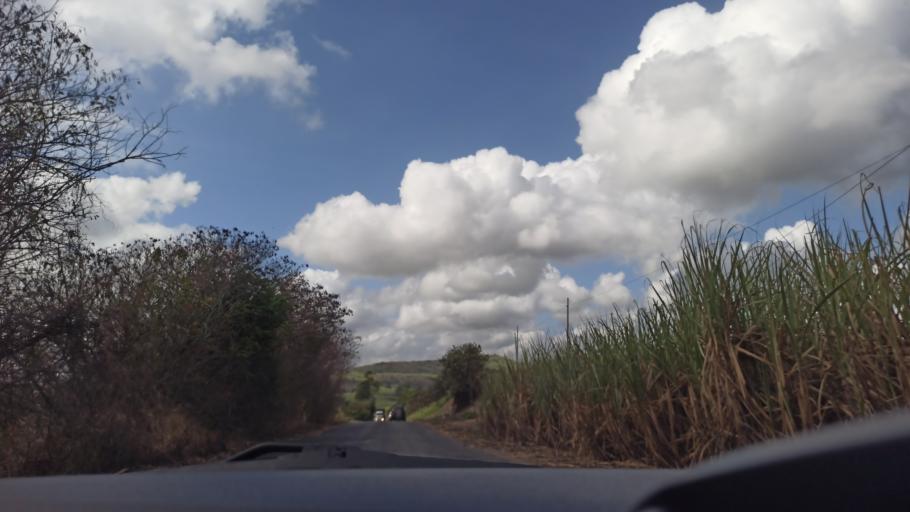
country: BR
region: Paraiba
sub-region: Juripiranga
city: Juripiranga
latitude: -7.4074
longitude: -35.2600
